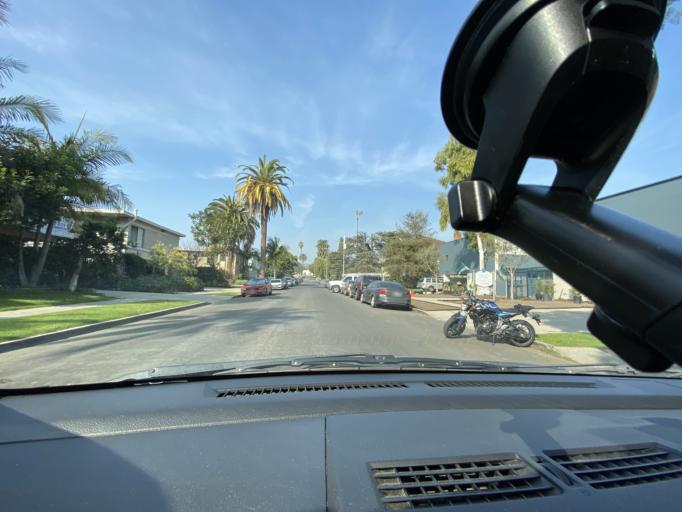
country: US
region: California
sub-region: Los Angeles County
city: Culver City
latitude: 34.0263
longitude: -118.4055
